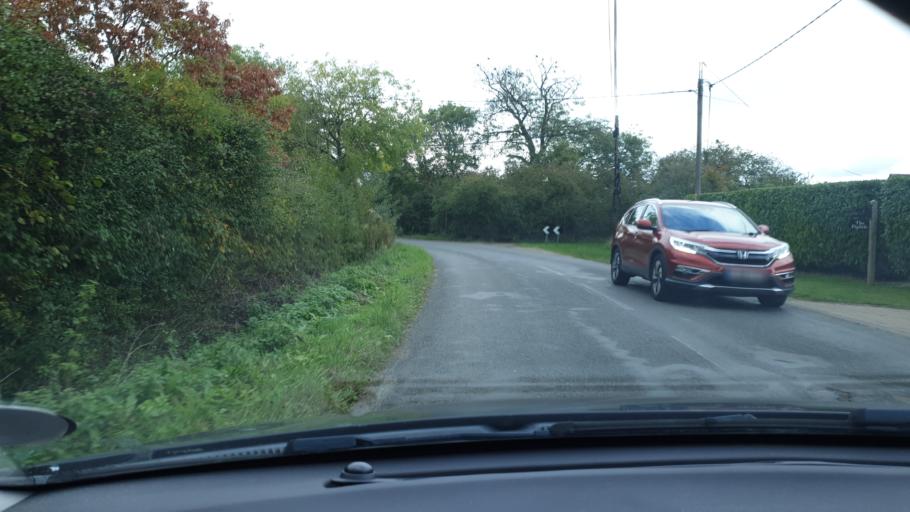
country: GB
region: England
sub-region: Essex
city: Mistley
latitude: 51.9360
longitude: 1.0955
